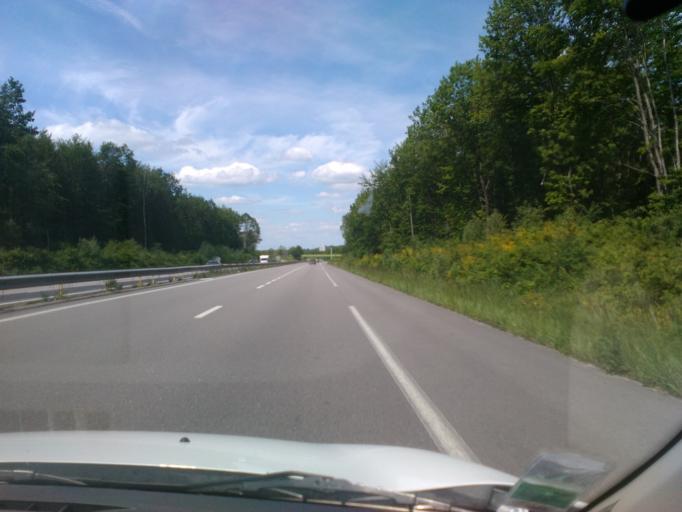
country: FR
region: Lorraine
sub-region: Departement des Vosges
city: Nomexy
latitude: 48.2896
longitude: 6.3779
